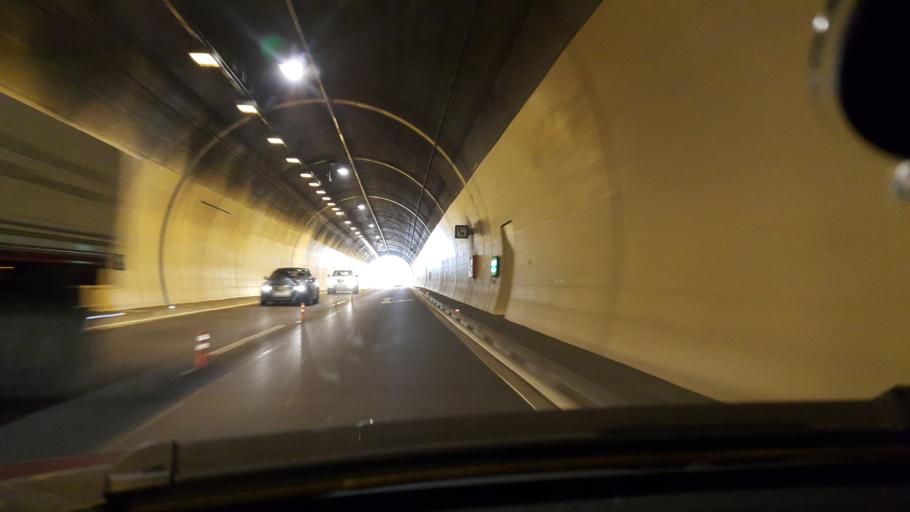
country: AT
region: Carinthia
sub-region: Klagenfurt am Woerthersee
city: Klagenfurt am Woerthersee
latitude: 46.6367
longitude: 14.2472
